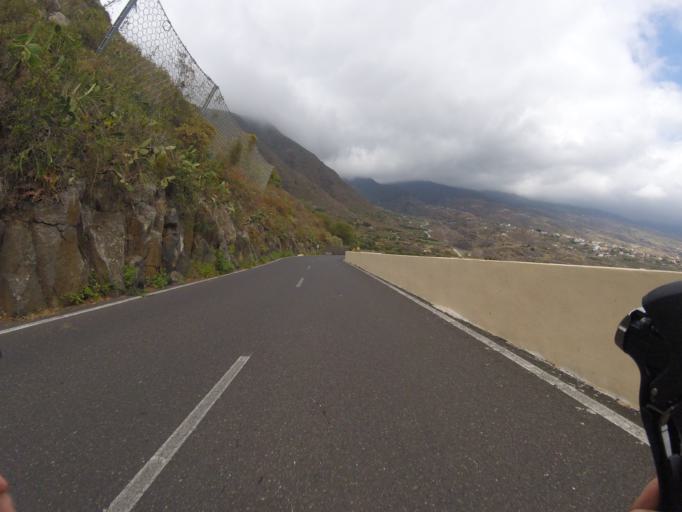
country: ES
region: Canary Islands
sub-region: Provincia de Santa Cruz de Tenerife
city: Guimar
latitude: 28.2960
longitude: -16.4133
